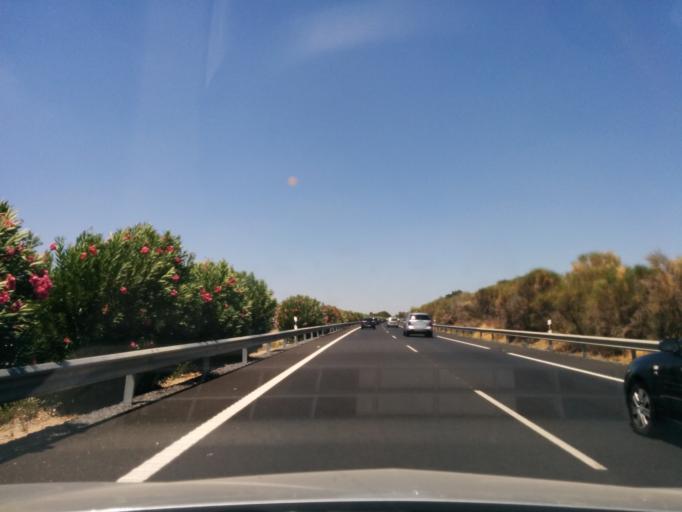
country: ES
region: Andalusia
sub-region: Provincia de Huelva
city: Villalba del Alcor
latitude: 37.3513
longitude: -6.4830
